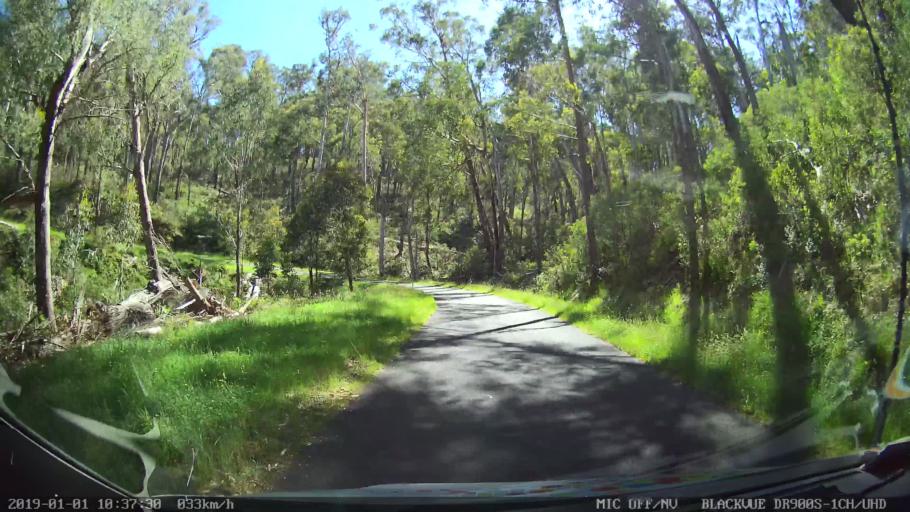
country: AU
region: New South Wales
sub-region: Snowy River
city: Jindabyne
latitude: -36.0487
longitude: 148.3045
